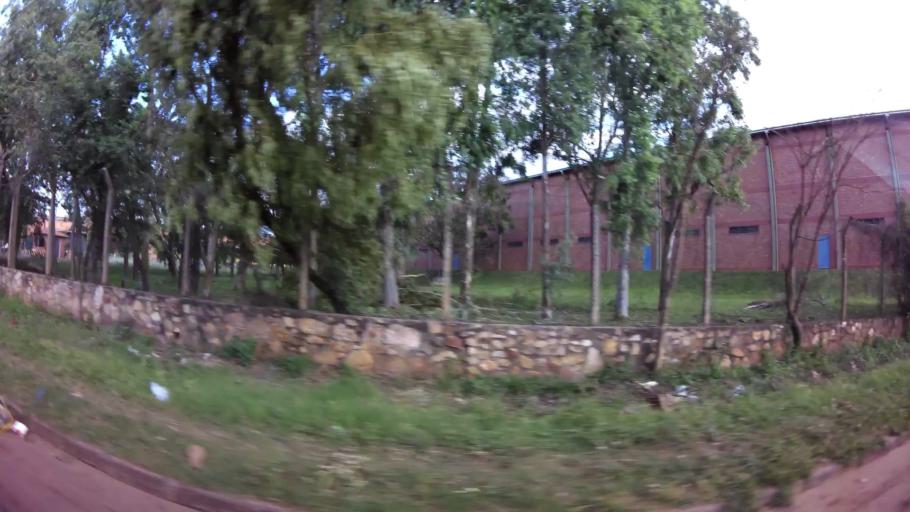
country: PY
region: Central
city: Fernando de la Mora
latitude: -25.3486
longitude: -57.5291
